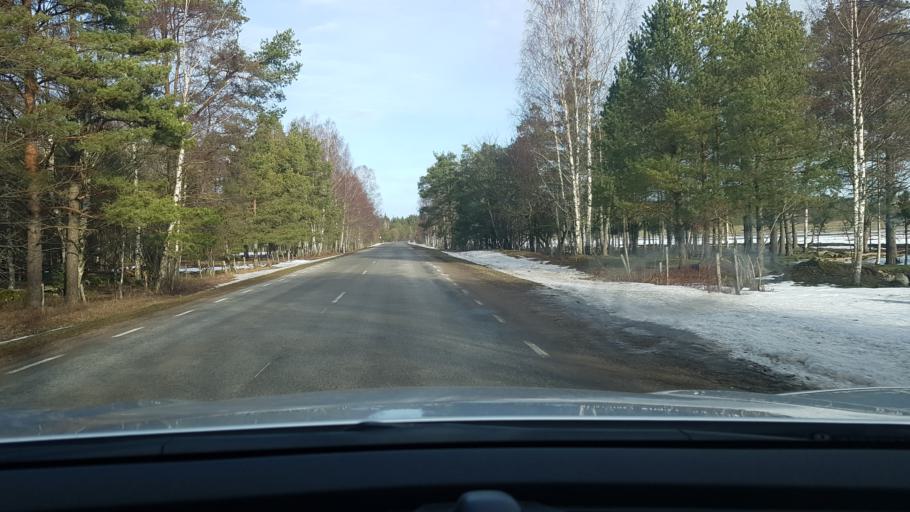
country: EE
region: Saare
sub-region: Kuressaare linn
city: Kuressaare
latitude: 58.4756
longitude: 22.7032
